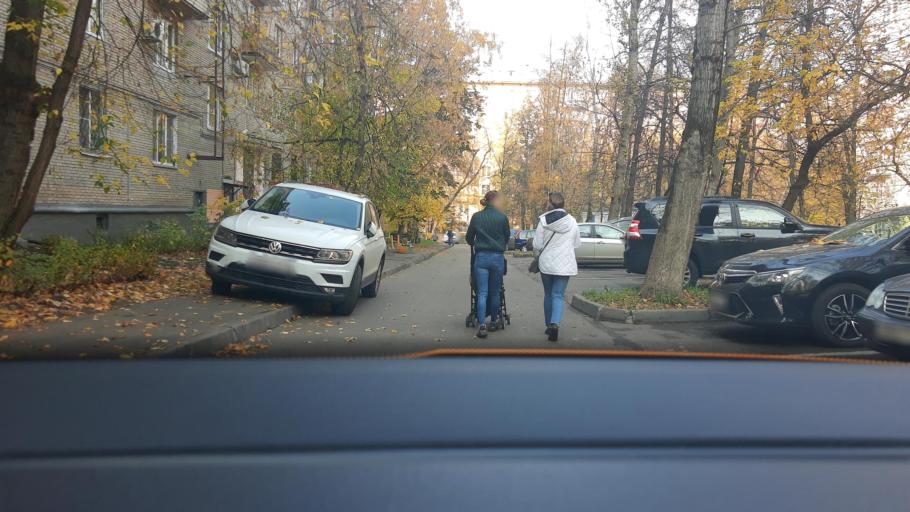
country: RU
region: Moskovskaya
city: Semenovskoye
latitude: 55.6785
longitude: 37.5269
